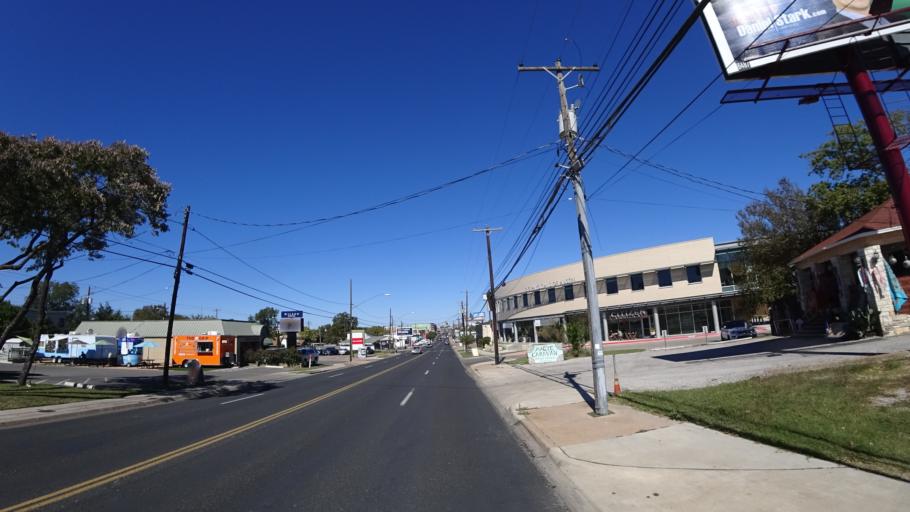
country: US
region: Texas
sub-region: Travis County
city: Austin
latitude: 30.3211
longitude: -97.7392
